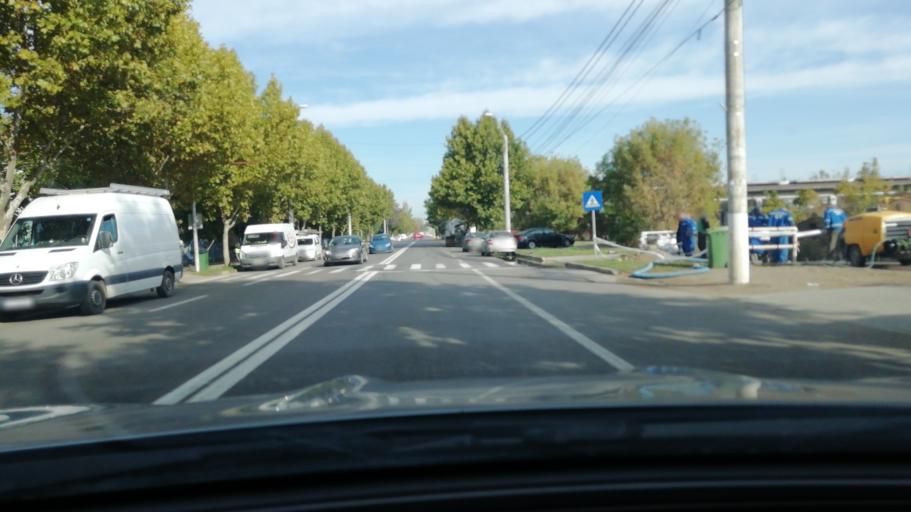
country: RO
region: Galati
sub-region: Municipiul Tecuci
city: Tecuci
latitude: 45.8205
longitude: 27.4391
